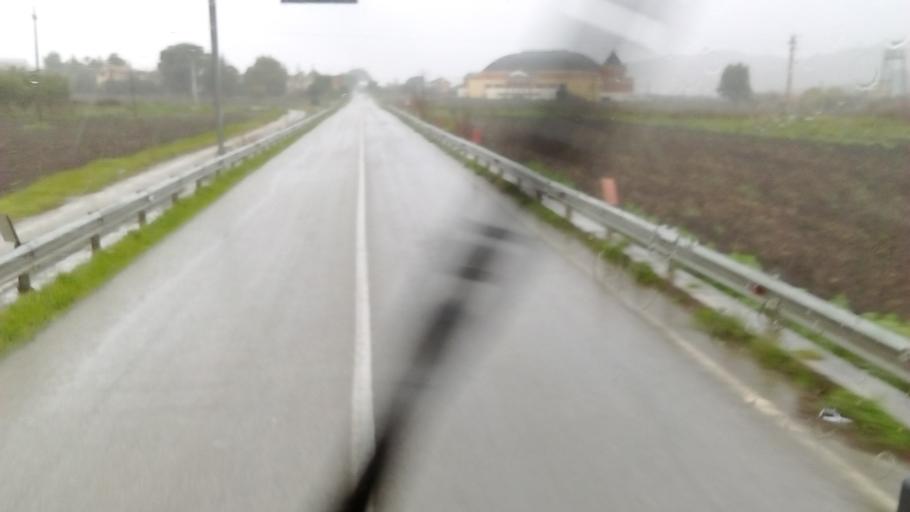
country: IT
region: Sicily
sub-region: Enna
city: Pietraperzia
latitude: 37.4193
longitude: 14.1732
